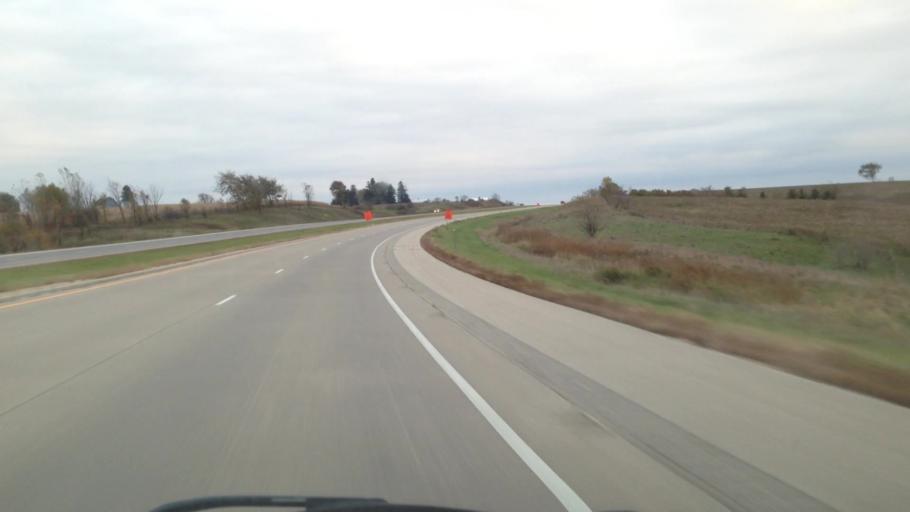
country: US
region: Minnesota
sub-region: Winona County
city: Winona
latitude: 43.9560
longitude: -91.6583
